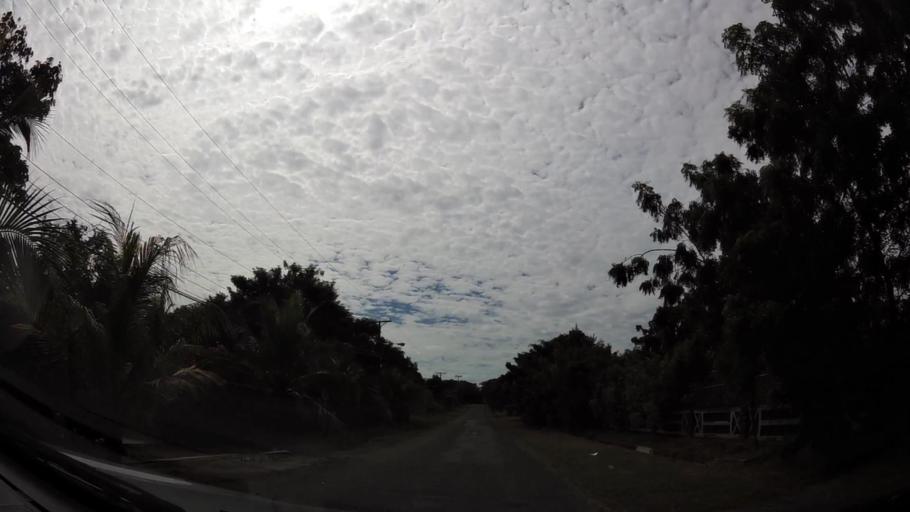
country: PA
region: Panama
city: Nueva Gorgona
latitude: 8.5380
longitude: -79.8988
